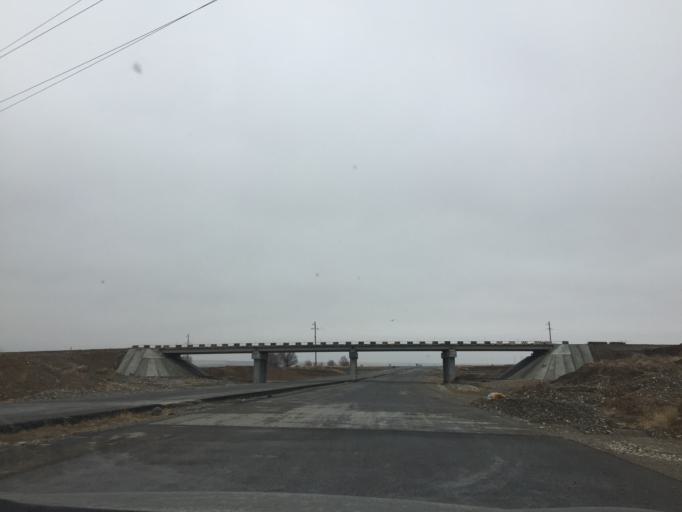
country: KZ
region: Ongtustik Qazaqstan
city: Turar Ryskulov
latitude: 42.5223
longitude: 70.3176
